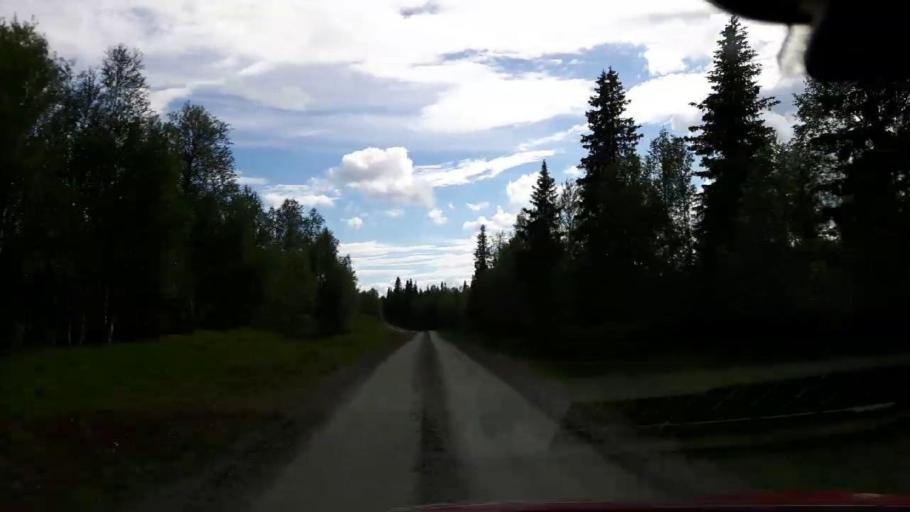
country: SE
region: Jaemtland
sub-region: Krokoms Kommun
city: Valla
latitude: 63.8690
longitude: 14.1188
